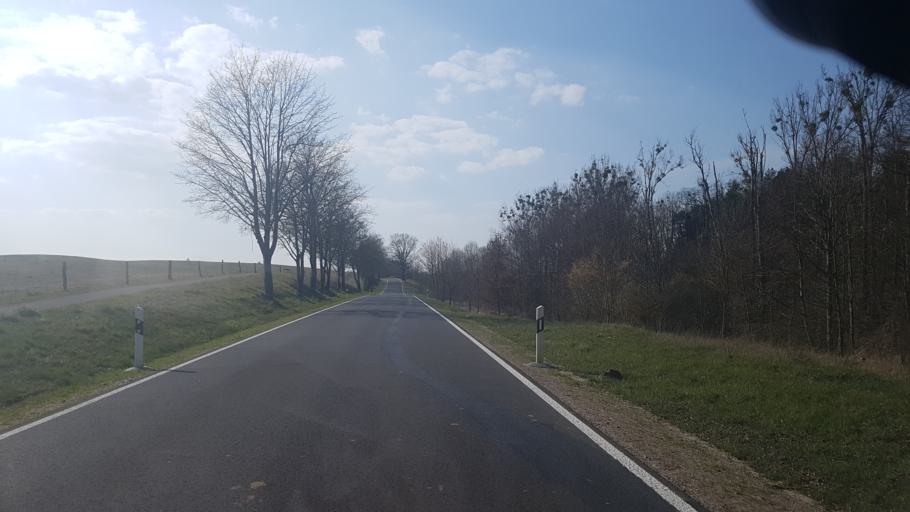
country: DE
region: Brandenburg
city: Gerswalde
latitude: 53.1738
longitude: 13.7900
